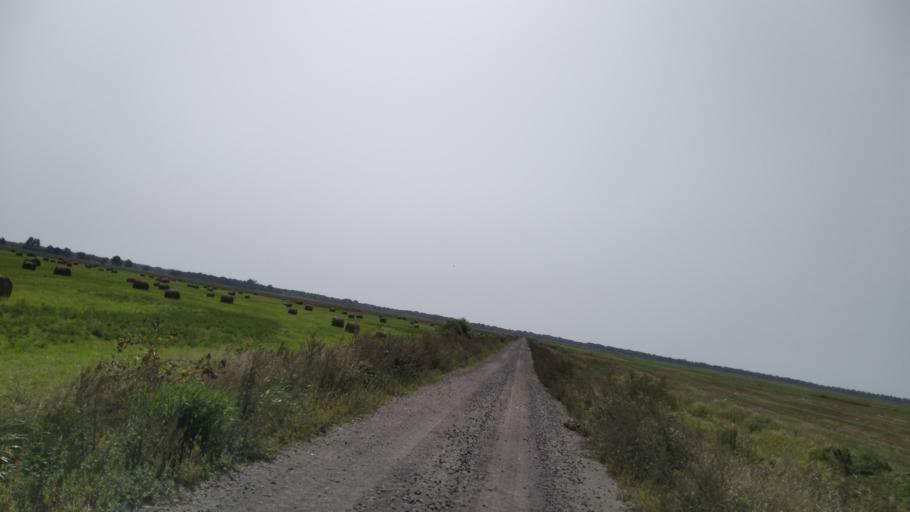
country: BY
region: Brest
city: Davyd-Haradok
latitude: 51.9899
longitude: 27.1759
